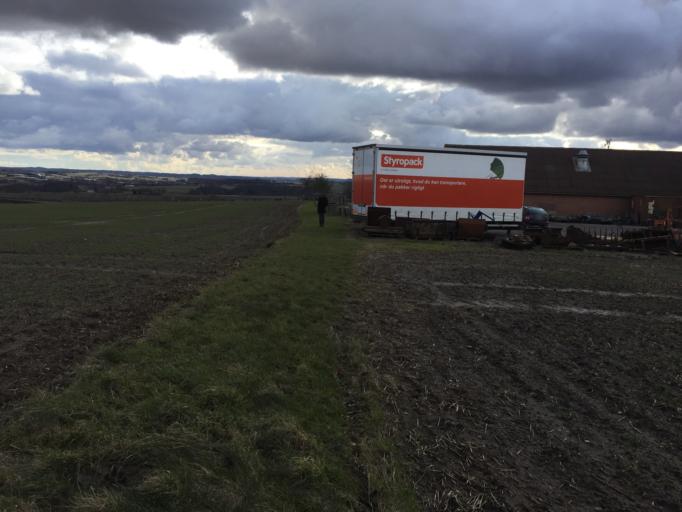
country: DK
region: Central Jutland
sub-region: Skanderborg Kommune
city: Ry
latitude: 56.1807
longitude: 9.7905
